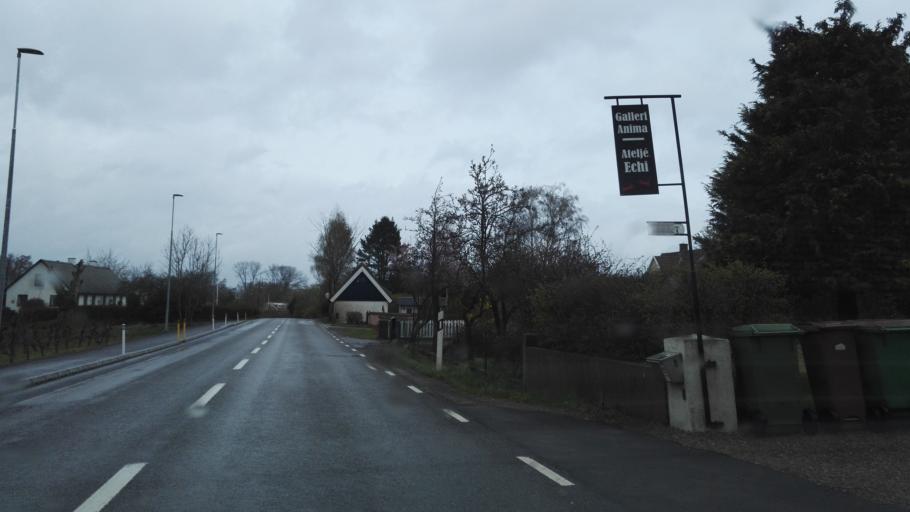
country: SE
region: Skane
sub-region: Simrishamns Kommun
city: Kivik
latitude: 55.6764
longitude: 14.2287
